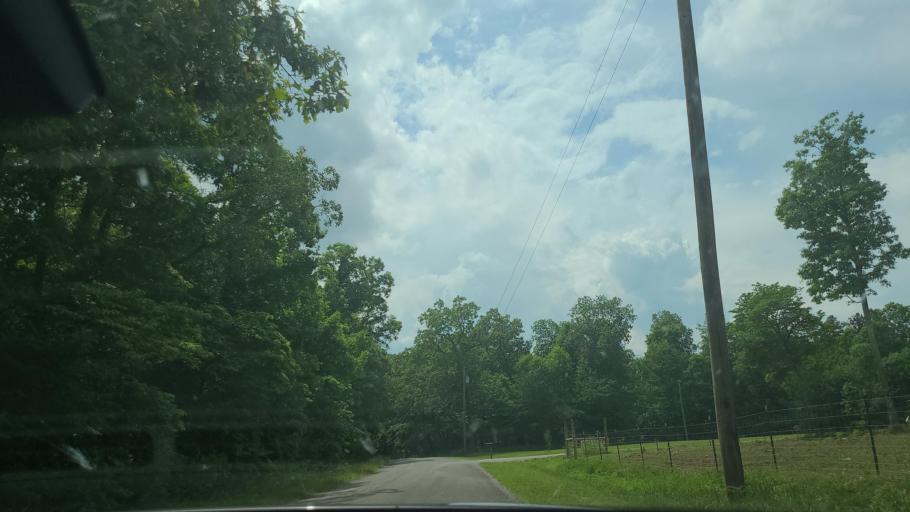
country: US
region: Tennessee
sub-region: Cumberland County
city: Lake Tansi
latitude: 35.7674
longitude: -85.0612
